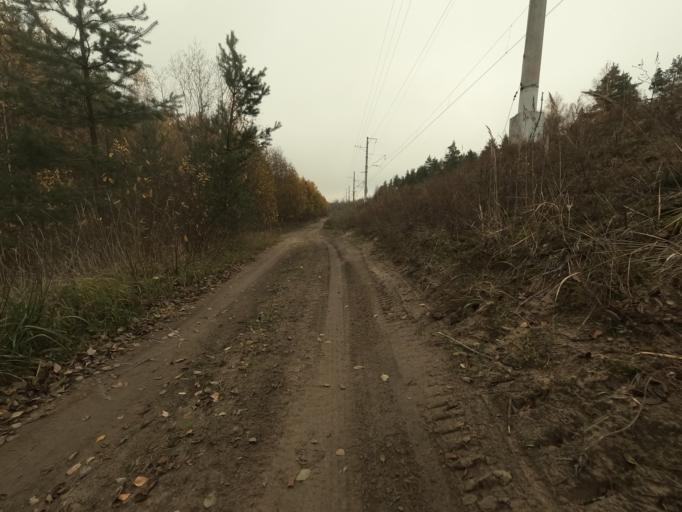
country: RU
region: Leningrad
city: Pavlovo
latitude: 59.7800
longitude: 30.8976
